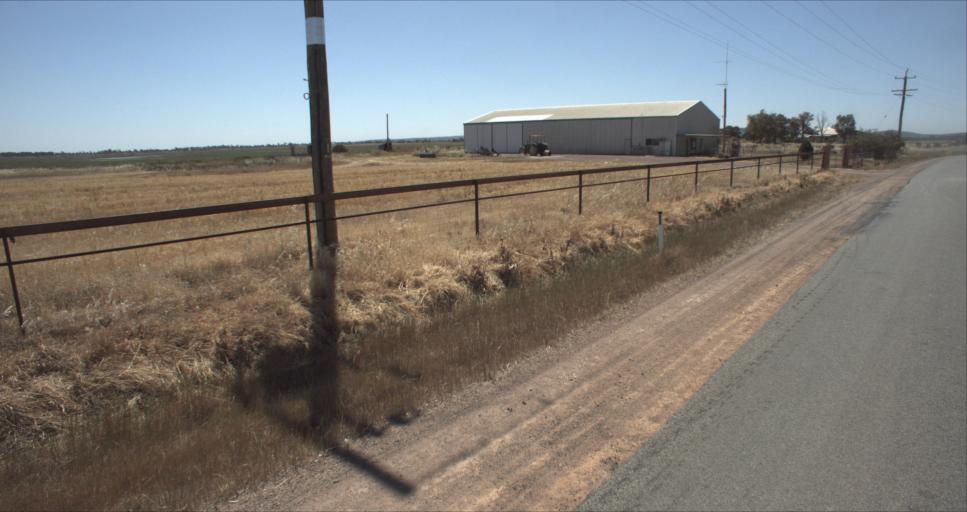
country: AU
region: New South Wales
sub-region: Leeton
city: Leeton
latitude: -34.5387
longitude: 146.4421
